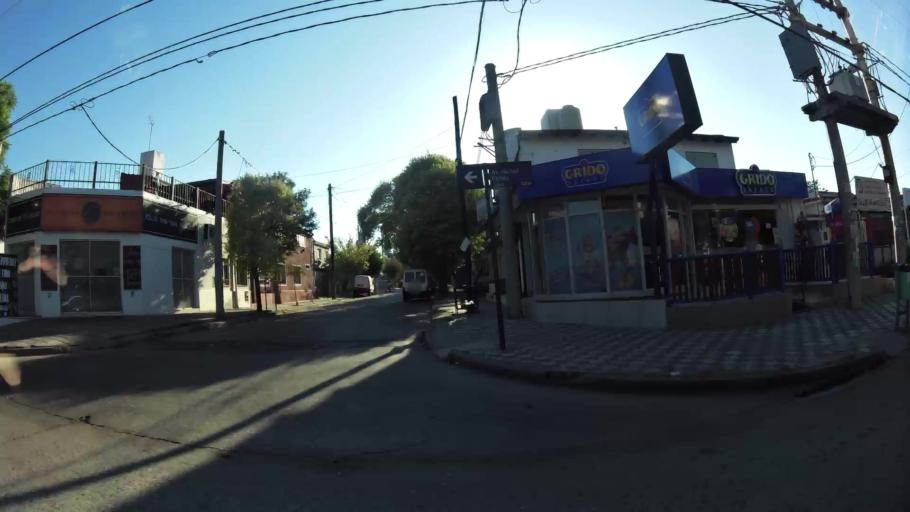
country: AR
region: Cordoba
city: Villa Allende
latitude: -31.3447
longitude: -64.2515
